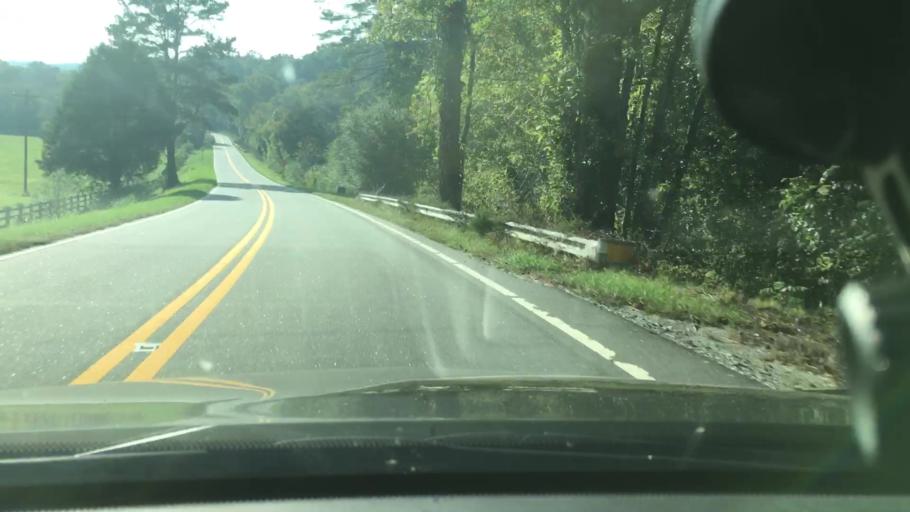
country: US
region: North Carolina
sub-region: Rutherford County
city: Rutherfordton
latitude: 35.3269
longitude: -82.0692
